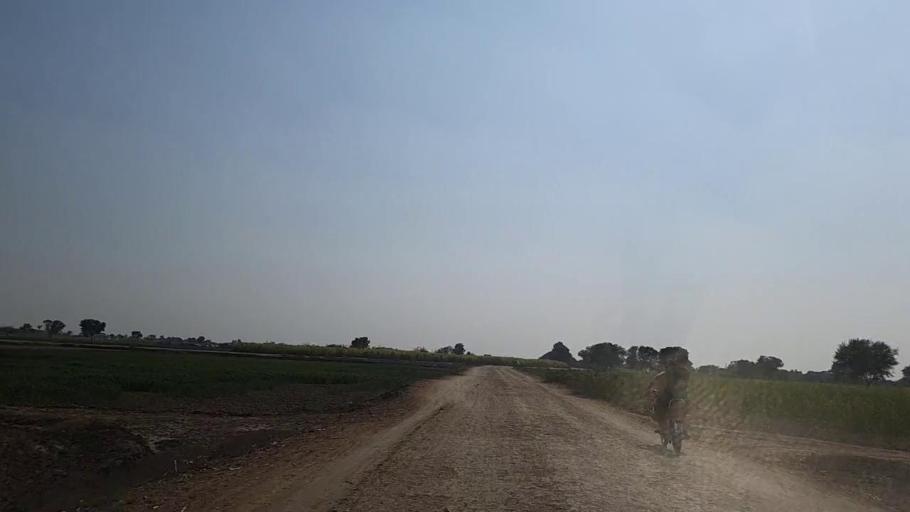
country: PK
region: Sindh
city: Daur
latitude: 26.4711
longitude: 68.2509
